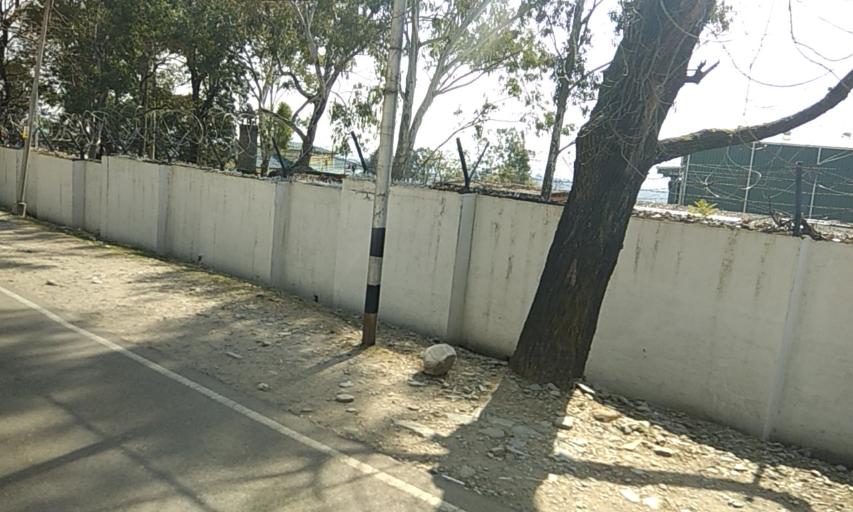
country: IN
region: Himachal Pradesh
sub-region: Kangra
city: Dharmsala
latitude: 32.1804
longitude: 76.3770
